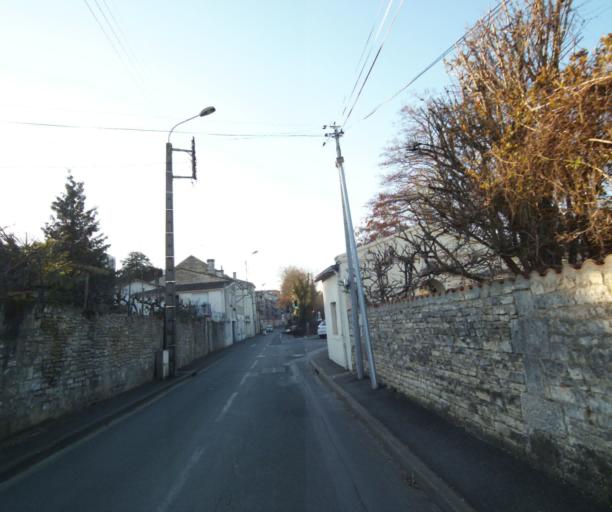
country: FR
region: Poitou-Charentes
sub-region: Departement des Deux-Sevres
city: Niort
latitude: 46.3235
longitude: -0.4731
